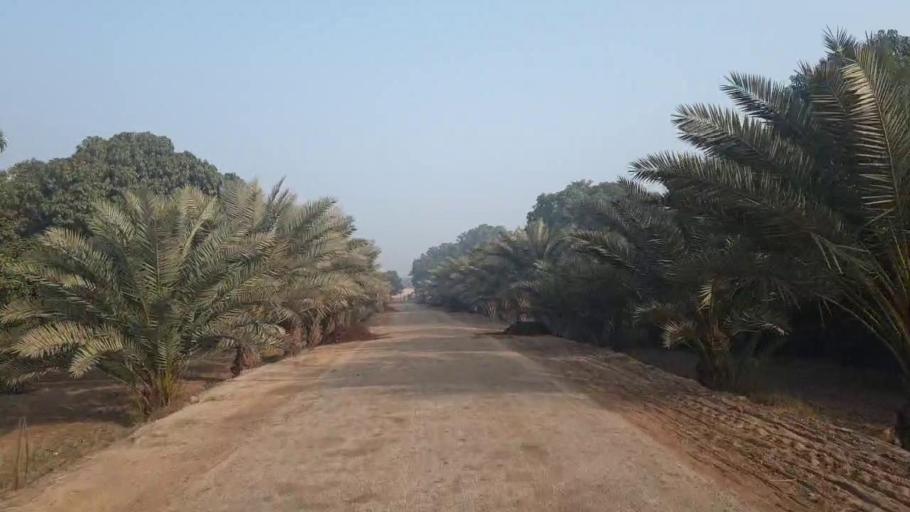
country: PK
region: Sindh
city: Tando Adam
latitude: 25.7922
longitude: 68.6403
